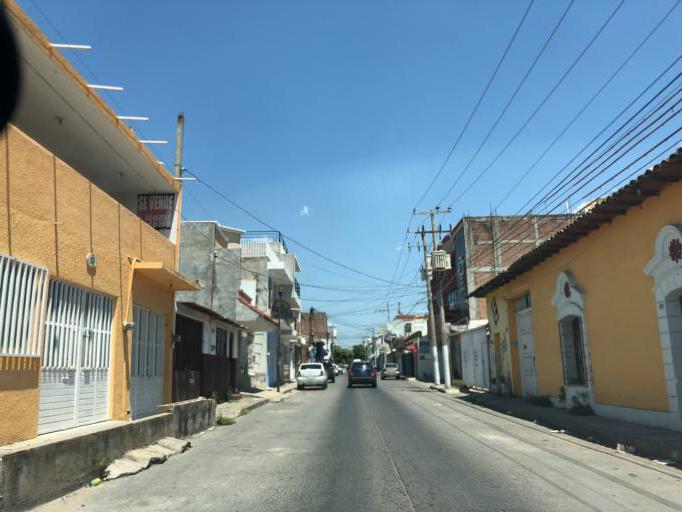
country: MX
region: Chiapas
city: Tuxtla Gutierrez
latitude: 16.7564
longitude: -93.1218
